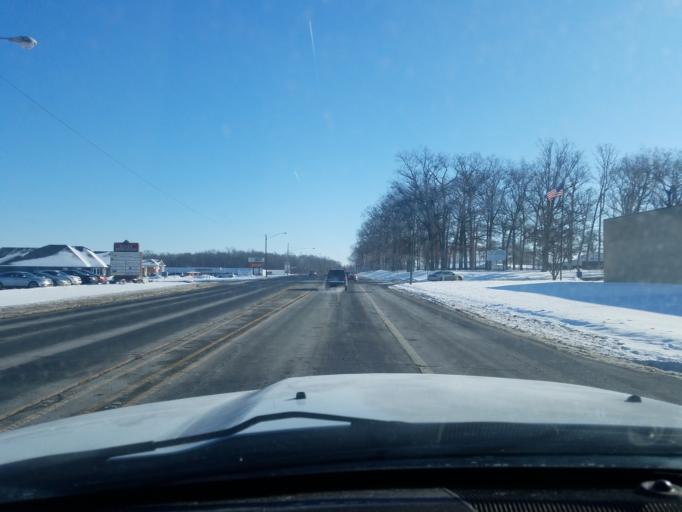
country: US
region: Indiana
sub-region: Noble County
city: Kendallville
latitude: 41.4522
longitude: -85.2567
